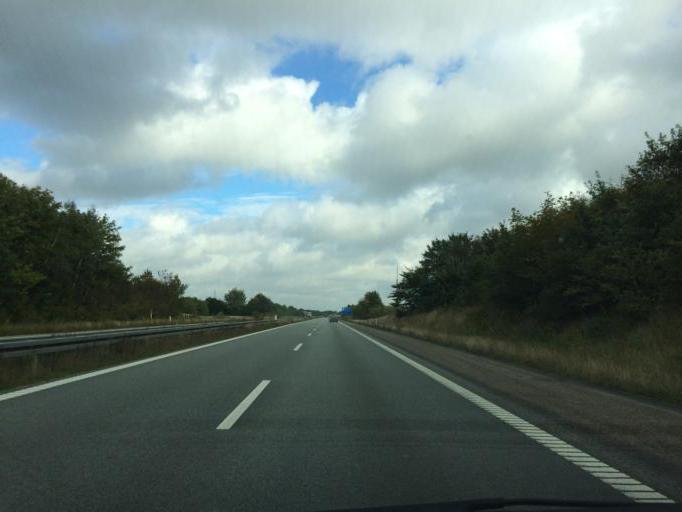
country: DK
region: North Denmark
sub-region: Alborg Kommune
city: Vodskov
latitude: 57.1259
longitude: 10.0737
